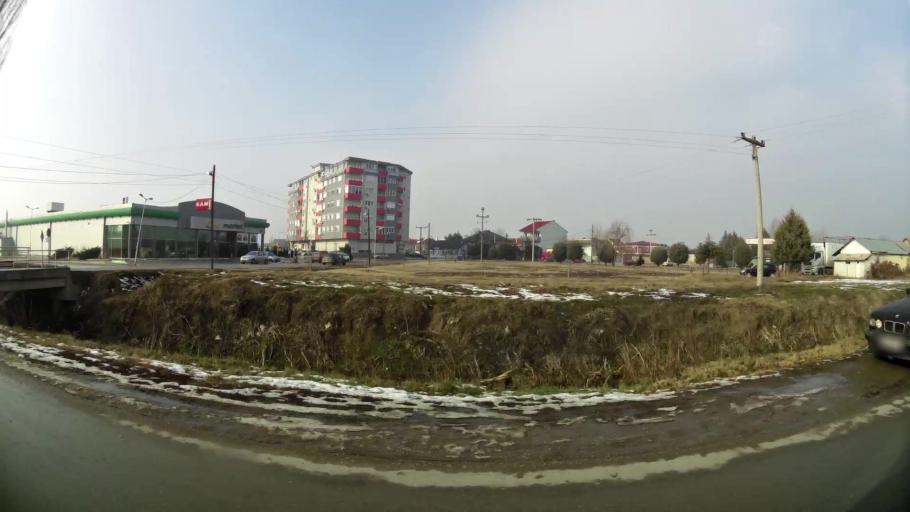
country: MK
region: Ilinden
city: Marino
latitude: 41.9898
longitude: 21.5870
